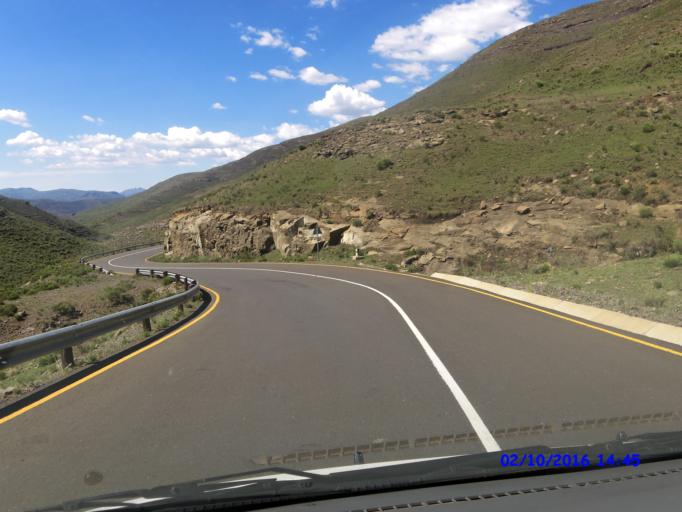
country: LS
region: Maseru
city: Nako
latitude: -29.5165
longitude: 28.0613
